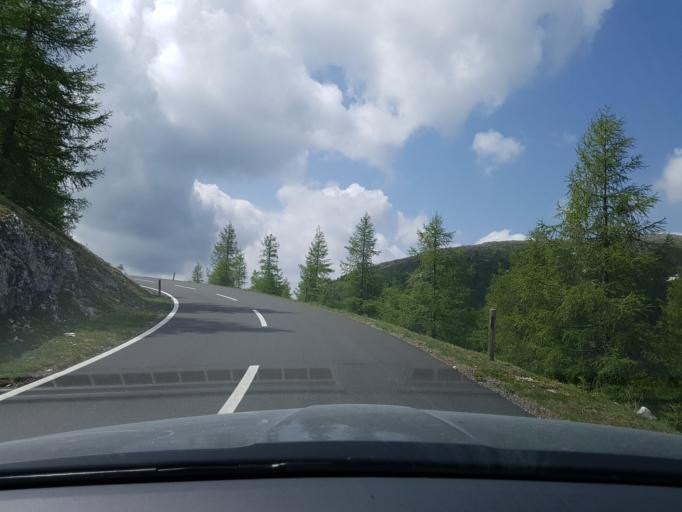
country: AT
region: Carinthia
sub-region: Politischer Bezirk Spittal an der Drau
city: Kleinkirchheim
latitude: 46.9406
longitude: 13.7483
